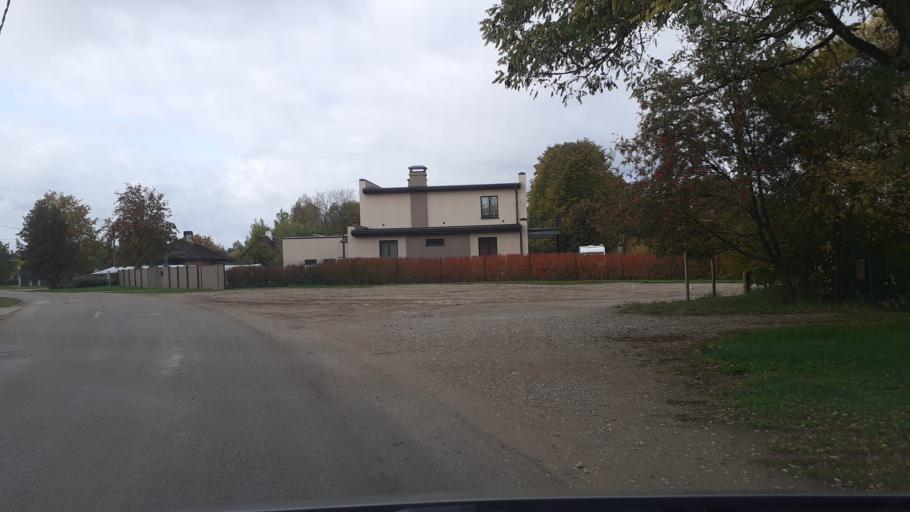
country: LV
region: Kuldigas Rajons
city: Kuldiga
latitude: 56.9664
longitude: 21.9921
